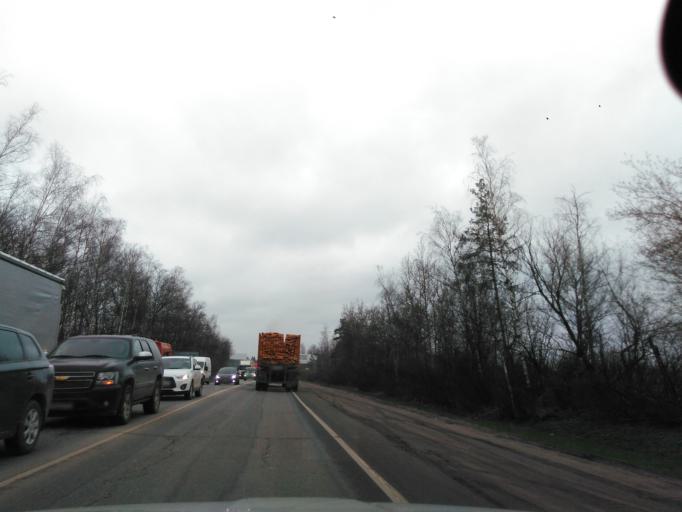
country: RU
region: Moskovskaya
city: Istra
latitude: 55.9028
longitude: 36.9449
